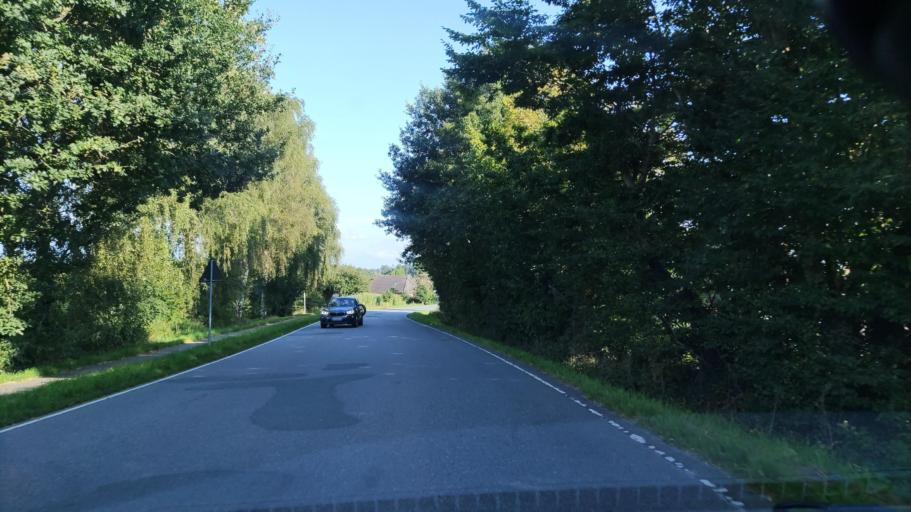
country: DE
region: Schleswig-Holstein
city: Willenscharen
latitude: 54.0173
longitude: 9.8009
